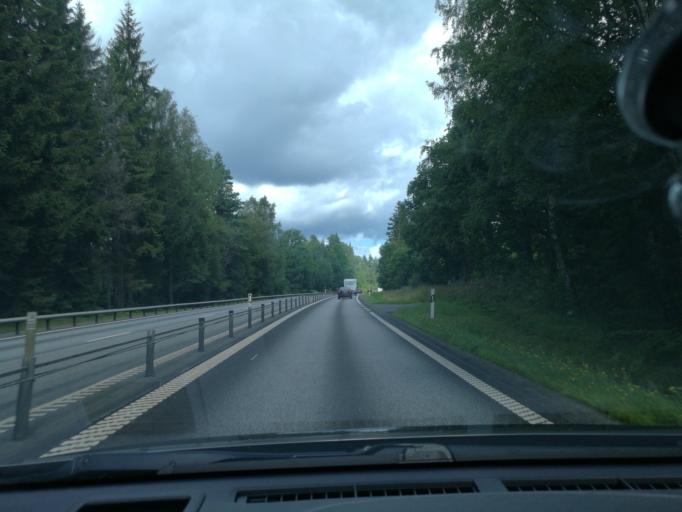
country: SE
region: Skane
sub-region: Osby Kommun
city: Osby
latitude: 56.3589
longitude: 14.0144
